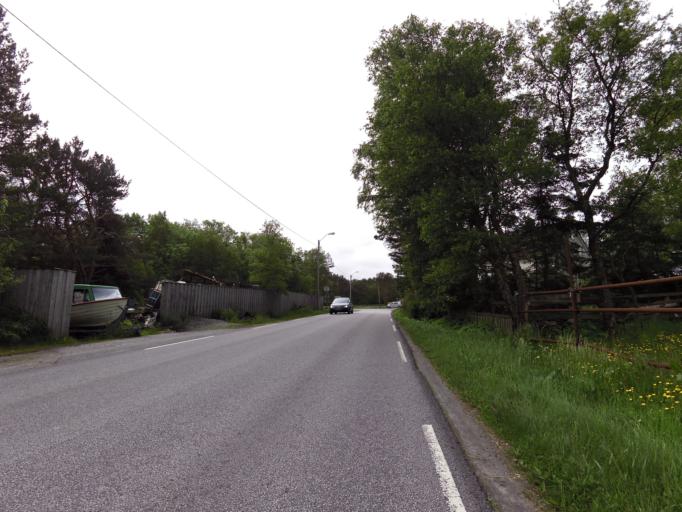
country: NO
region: Rogaland
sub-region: Sola
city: Sola
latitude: 58.8715
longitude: 5.6022
